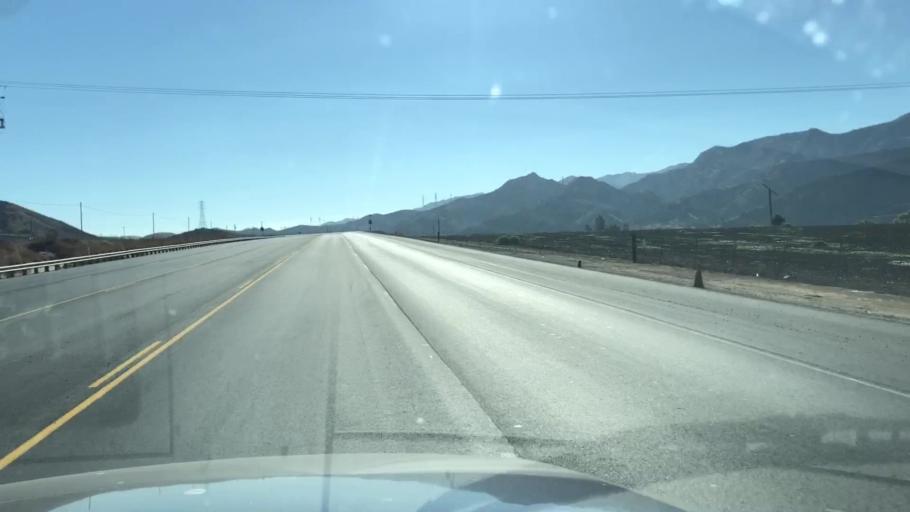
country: US
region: California
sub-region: Los Angeles County
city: Val Verde
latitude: 34.4033
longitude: -118.7127
